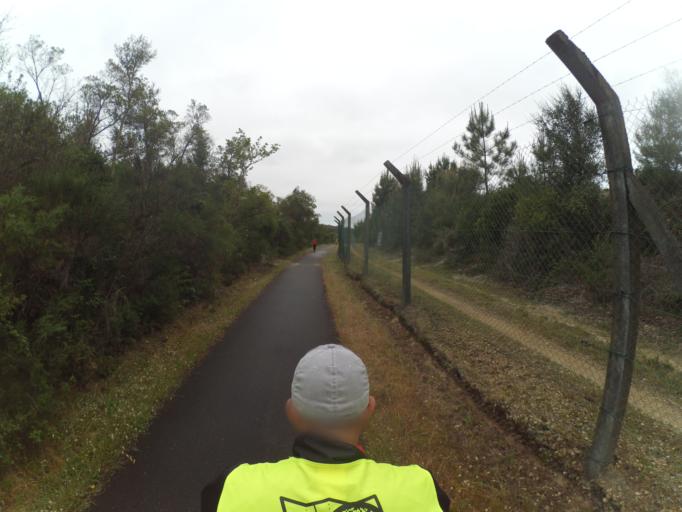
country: FR
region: Aquitaine
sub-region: Departement des Landes
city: Mimizan
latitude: 44.2226
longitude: -1.2666
